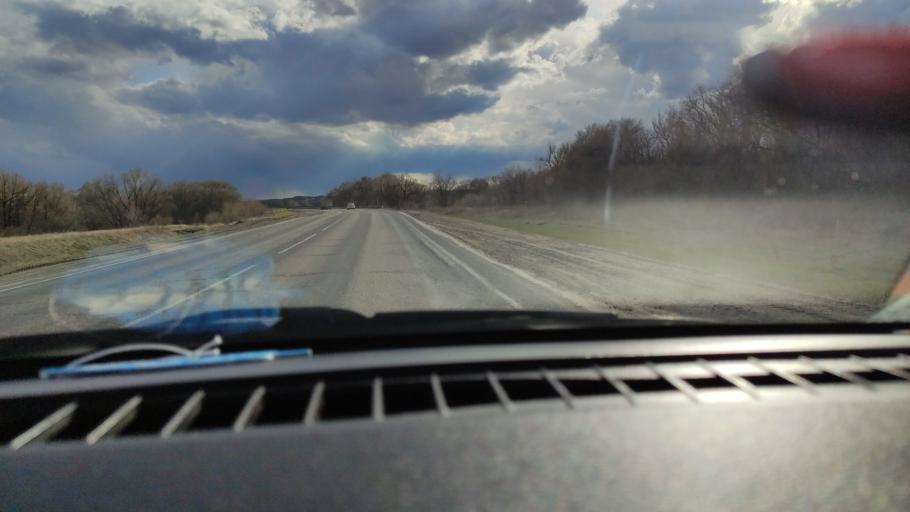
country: RU
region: Saratov
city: Sinodskoye
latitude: 51.9751
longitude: 46.6470
